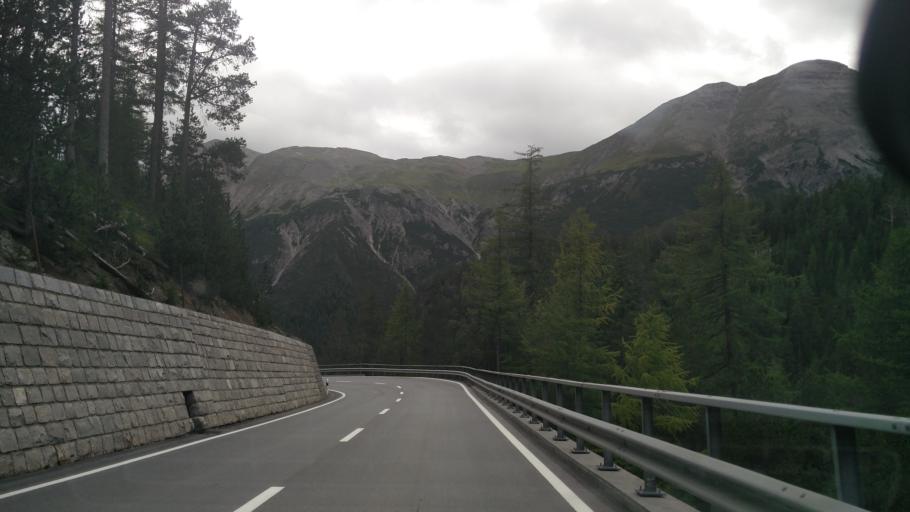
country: CH
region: Grisons
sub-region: Inn District
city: Zernez
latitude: 46.6784
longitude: 10.1653
